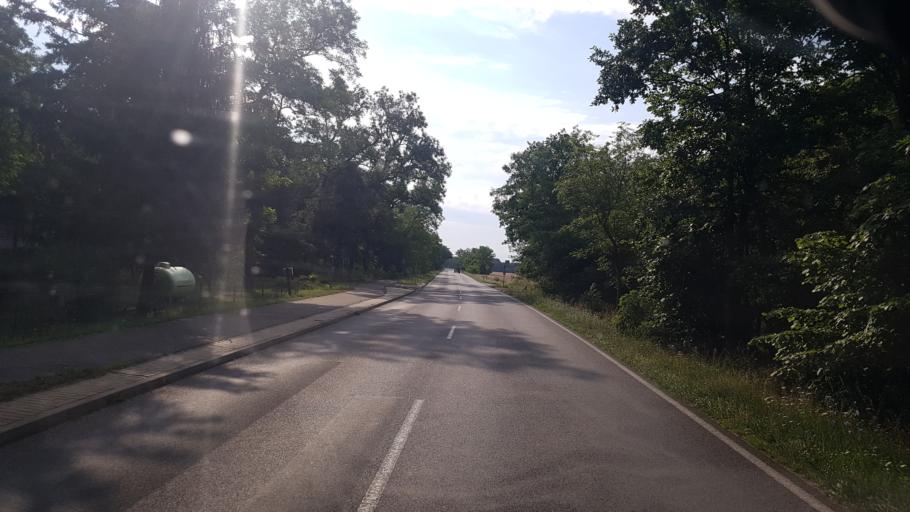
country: DE
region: Brandenburg
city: Baruth
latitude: 52.0555
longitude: 13.5679
